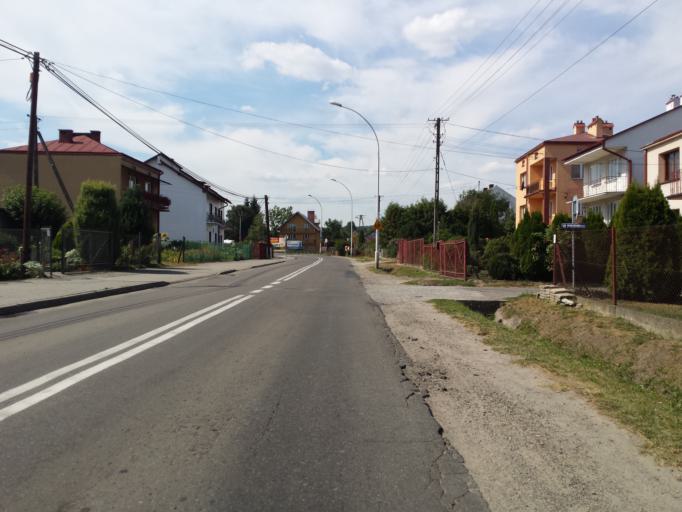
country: PL
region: Subcarpathian Voivodeship
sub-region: Przemysl
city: Przemysl
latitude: 49.7517
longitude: 22.7844
